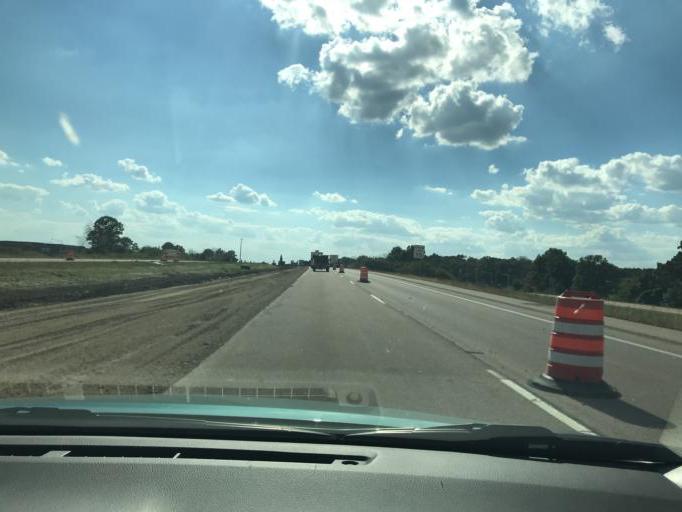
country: US
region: Wisconsin
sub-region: Rock County
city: Clinton
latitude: 42.5428
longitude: -88.9451
